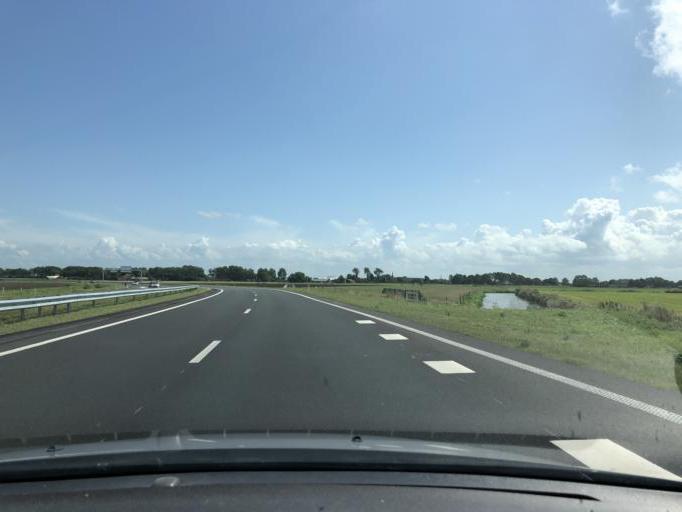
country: NL
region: North Holland
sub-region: Gemeente Medemblik
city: Medemblik
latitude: 52.6786
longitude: 5.1670
